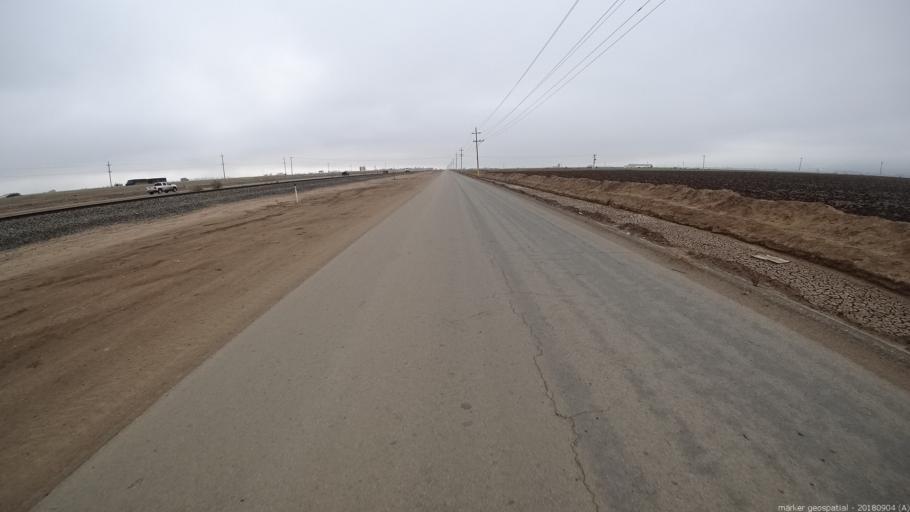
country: US
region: California
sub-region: Monterey County
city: Gonzales
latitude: 36.4815
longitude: -121.4153
